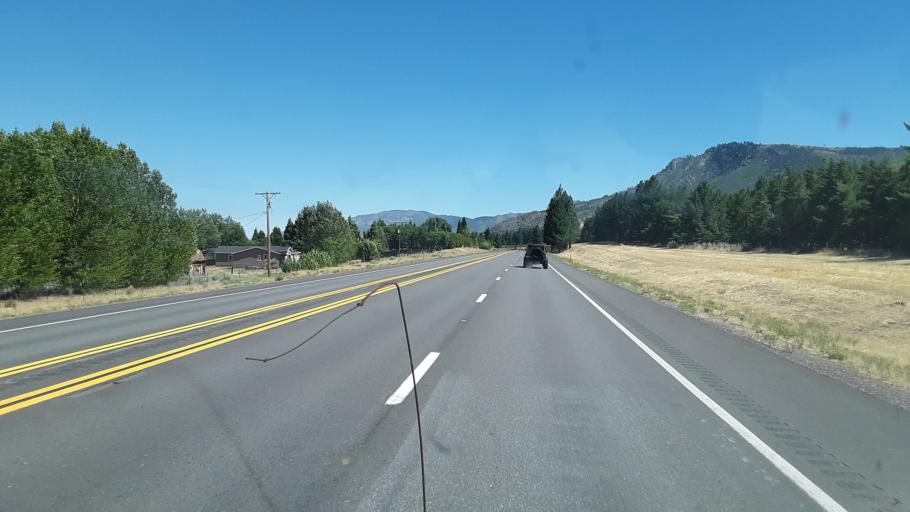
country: US
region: California
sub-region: Lassen County
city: Janesville
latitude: 40.2536
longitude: -120.4643
